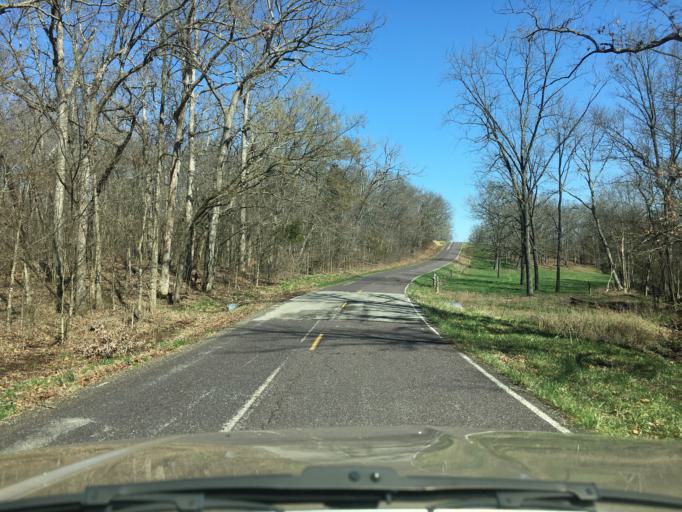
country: US
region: Missouri
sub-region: Franklin County
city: New Haven
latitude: 38.5423
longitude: -91.3303
